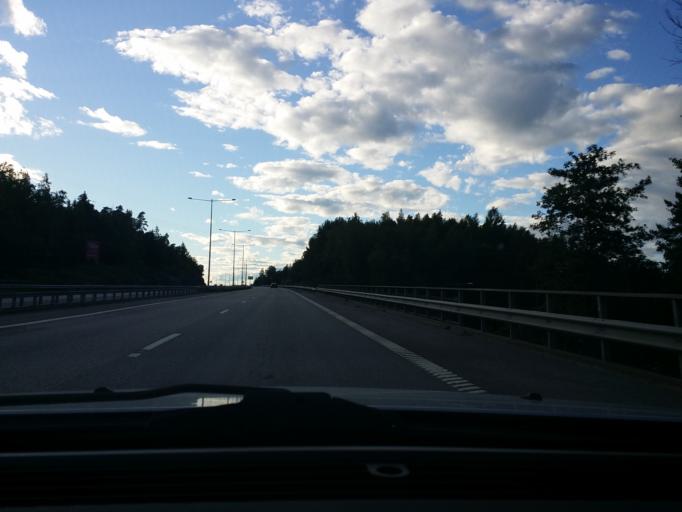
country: SE
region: Stockholm
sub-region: Upplands-Bro Kommun
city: Kungsaengen
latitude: 59.4959
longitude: 17.7448
